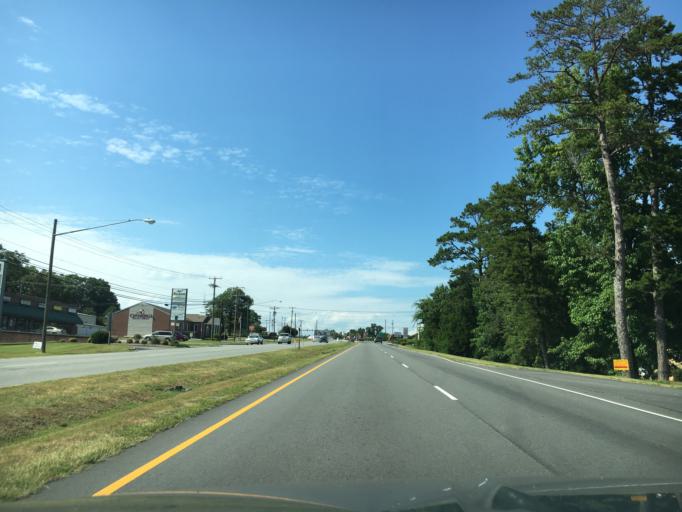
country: US
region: Virginia
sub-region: Halifax County
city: Halifax
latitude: 36.7316
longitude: -78.9183
